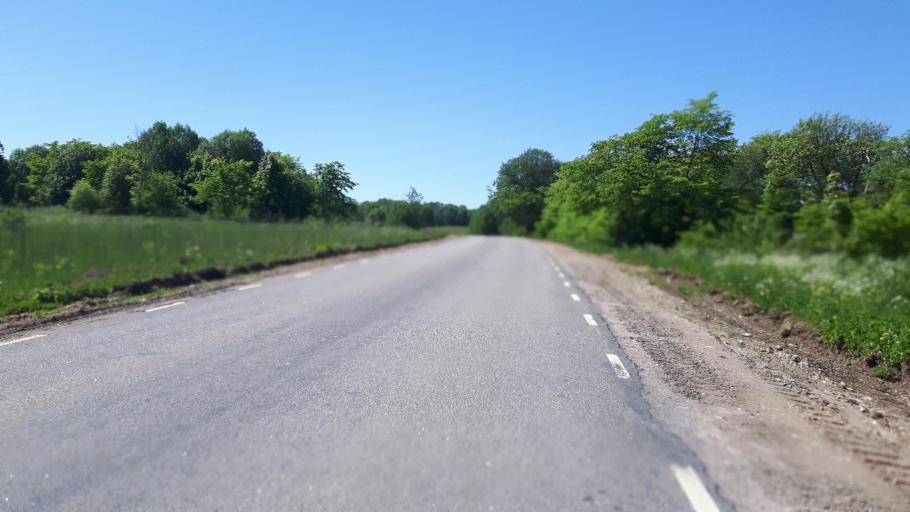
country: EE
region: Ida-Virumaa
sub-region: Narva-Joesuu linn
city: Narva-Joesuu
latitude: 59.4097
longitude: 27.9458
